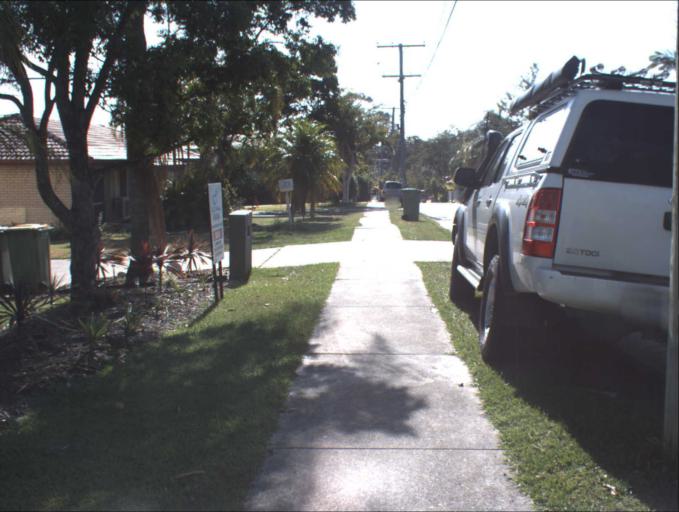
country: AU
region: Queensland
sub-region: Logan
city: Rochedale South
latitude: -27.5996
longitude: 153.1184
